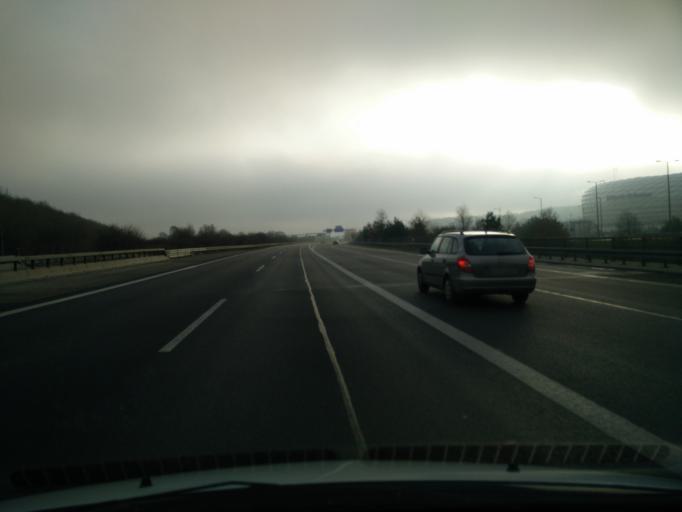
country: DE
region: Bavaria
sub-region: Upper Bavaria
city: Unterfoehring
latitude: 48.2244
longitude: 11.6209
